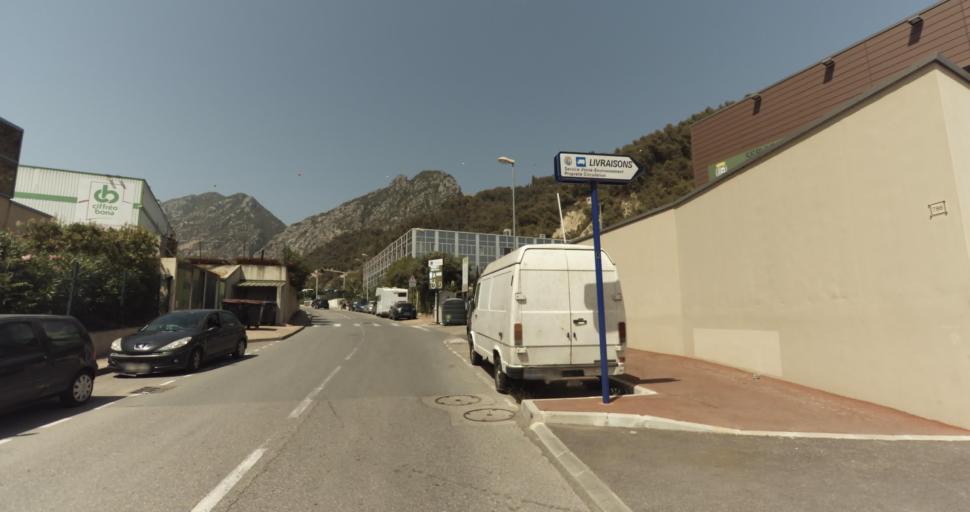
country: FR
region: Provence-Alpes-Cote d'Azur
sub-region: Departement des Alpes-Maritimes
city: Sainte-Agnes
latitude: 43.8057
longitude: 7.4876
